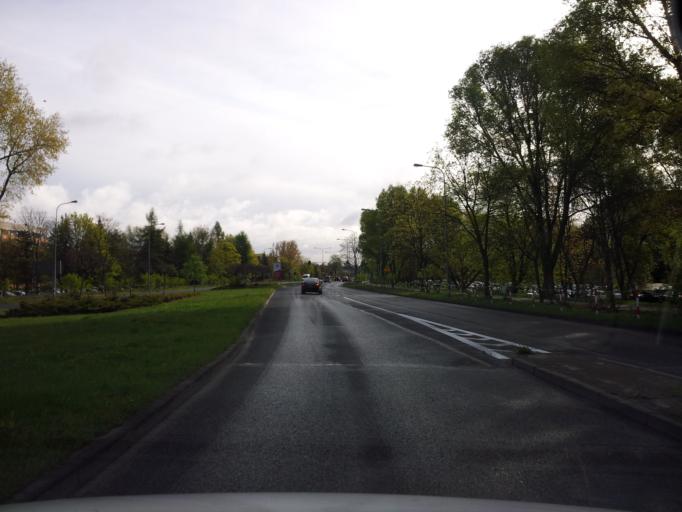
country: PL
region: Lubusz
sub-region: Zielona Gora
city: Zielona Gora
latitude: 51.9333
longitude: 15.4845
